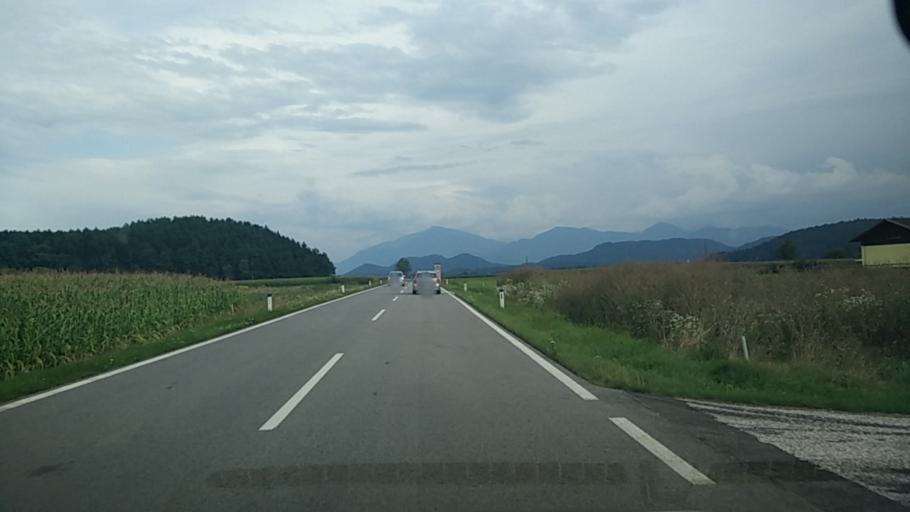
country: AT
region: Carinthia
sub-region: Politischer Bezirk Klagenfurt Land
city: Poggersdorf
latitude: 46.6452
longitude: 14.5127
